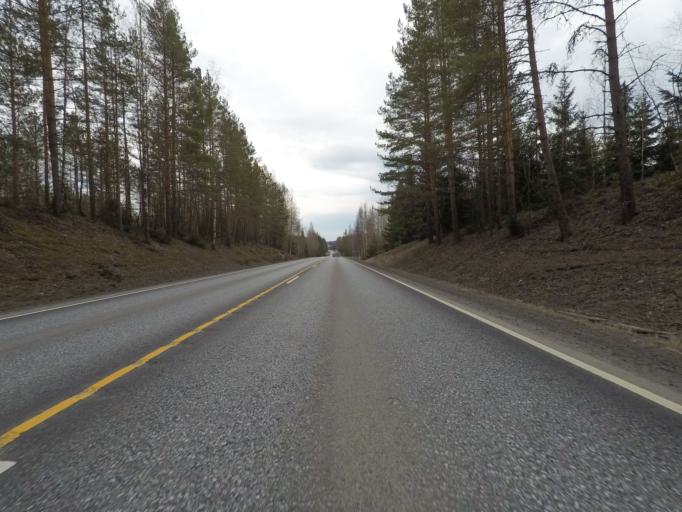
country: FI
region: Paijanne Tavastia
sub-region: Lahti
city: Hartola
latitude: 61.6356
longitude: 26.0168
